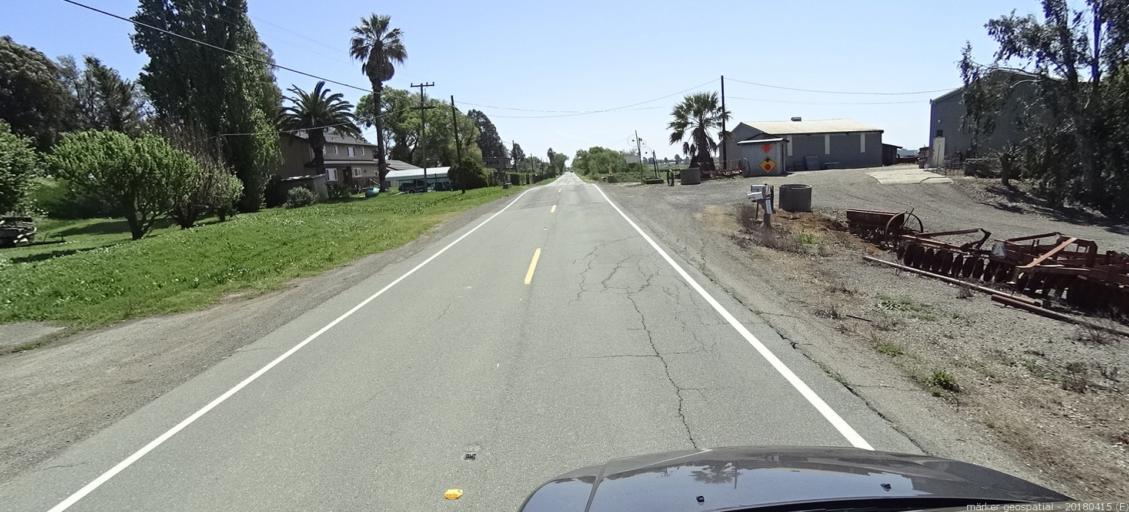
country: US
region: California
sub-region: Solano County
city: Rio Vista
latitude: 38.1348
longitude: -121.5947
